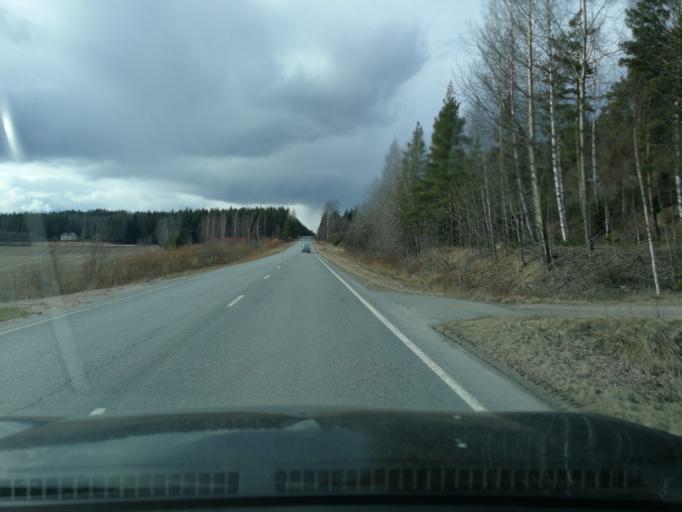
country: FI
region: Varsinais-Suomi
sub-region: Salo
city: Muurla
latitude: 60.3316
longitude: 23.2428
